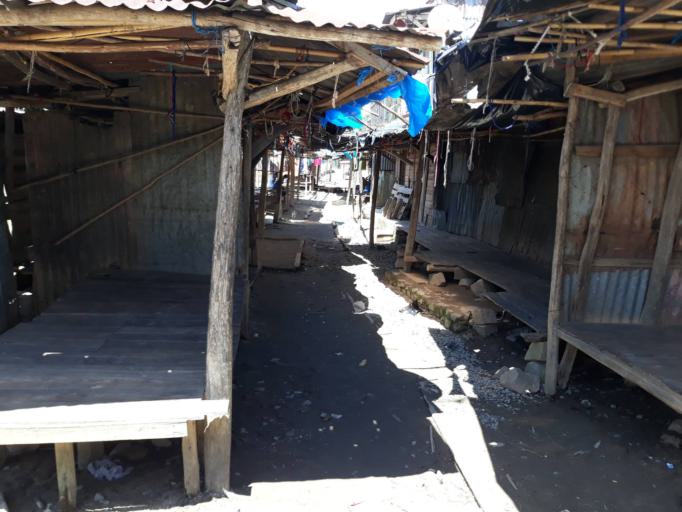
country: MG
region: Atsinanana
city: Ampasimanolotra
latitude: -18.8206
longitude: 49.0725
